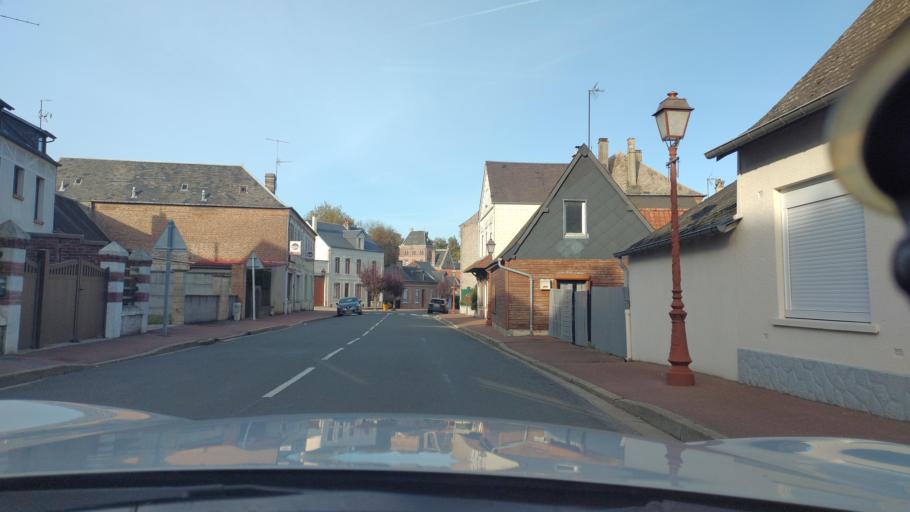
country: FR
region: Picardie
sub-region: Departement de la Somme
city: Fressenneville
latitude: 50.0686
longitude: 1.5767
